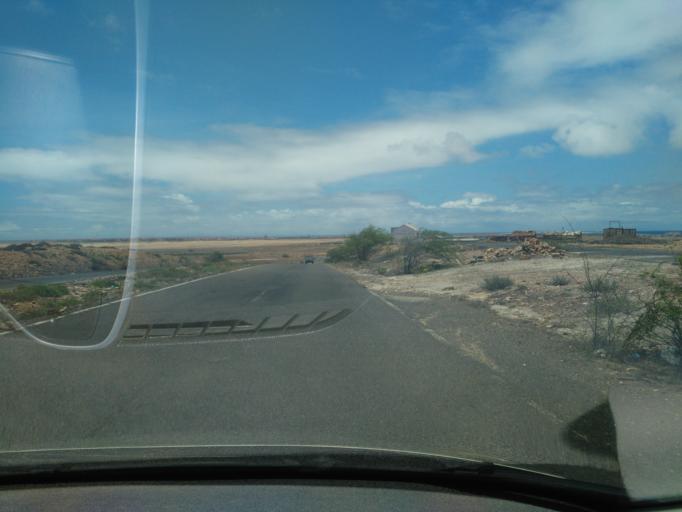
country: CV
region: Sal
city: Santa Maria
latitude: 16.6341
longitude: -22.9173
